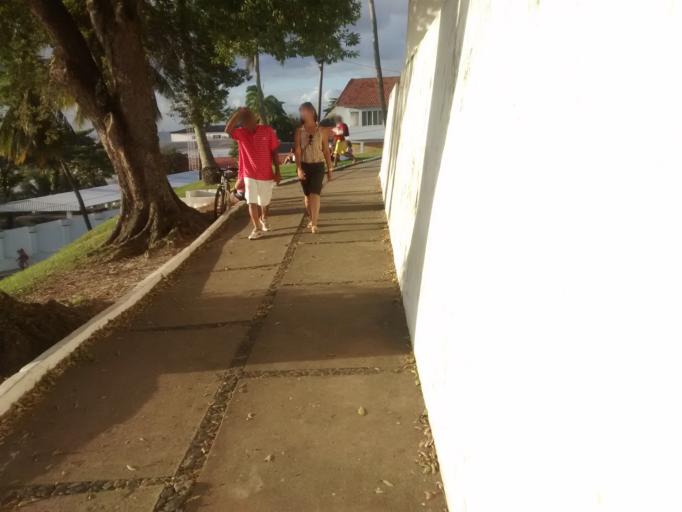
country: BR
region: Bahia
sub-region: Salvador
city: Salvador
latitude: -12.9299
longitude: -38.5178
